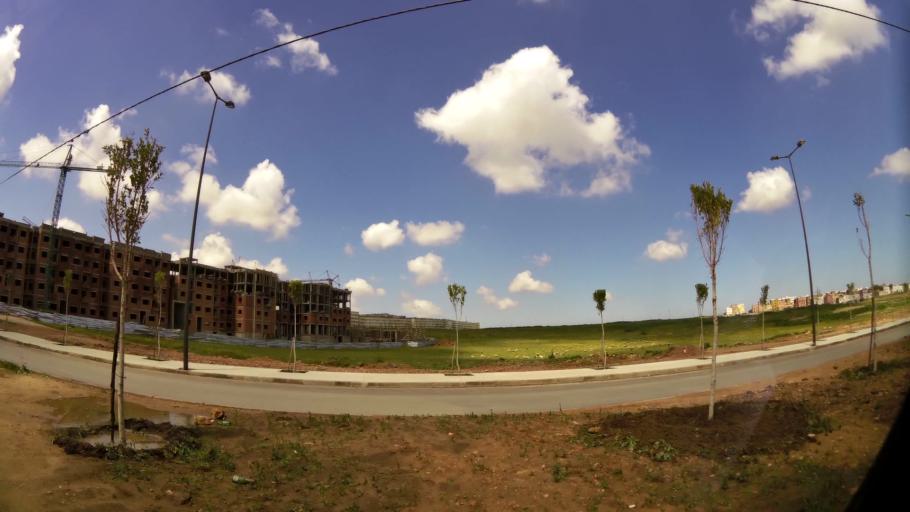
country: MA
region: Grand Casablanca
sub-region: Mediouna
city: Tit Mellil
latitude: 33.5383
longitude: -7.5458
